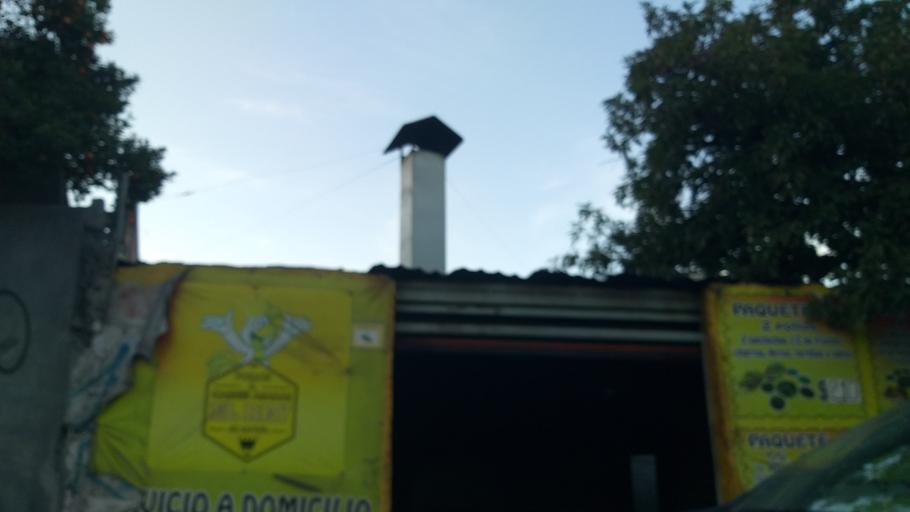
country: MX
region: Nuevo Leon
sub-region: Monterrey
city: Monterrey
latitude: 25.6383
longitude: -100.3086
